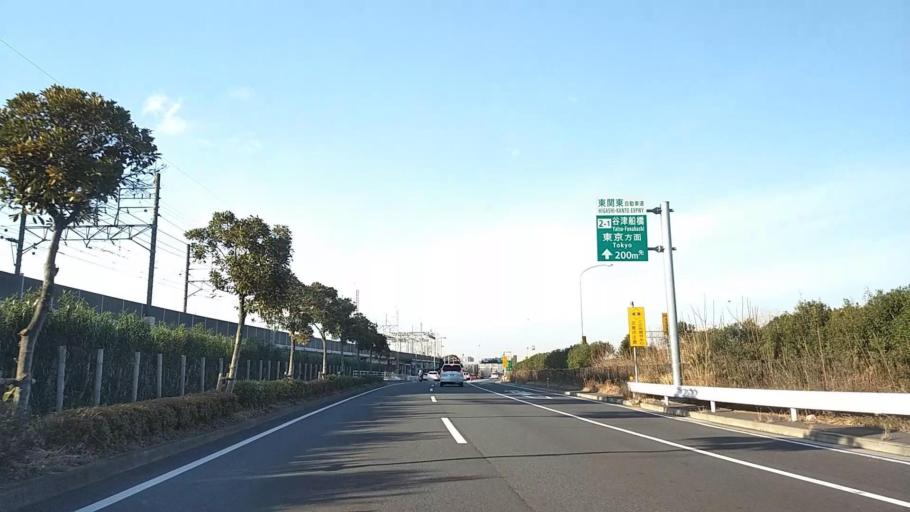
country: JP
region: Chiba
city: Funabashi
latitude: 35.6745
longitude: 140.0034
